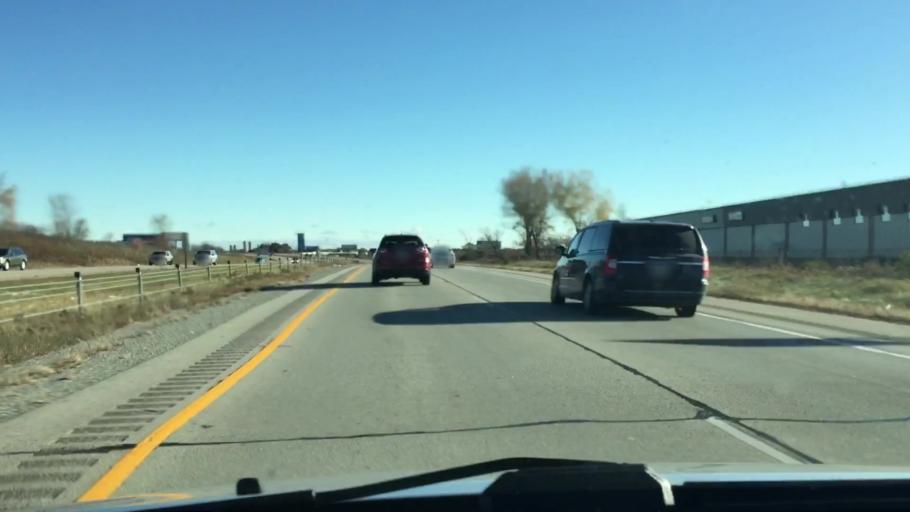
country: US
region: Wisconsin
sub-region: Outagamie County
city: Kaukauna
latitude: 44.3073
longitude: -88.2425
